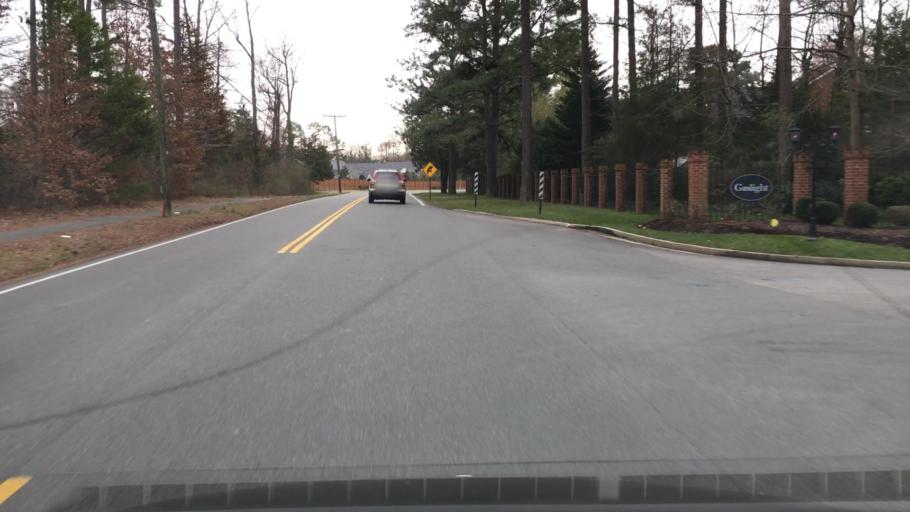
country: US
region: Virginia
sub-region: Henrico County
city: Tuckahoe
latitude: 37.5914
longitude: -77.5958
